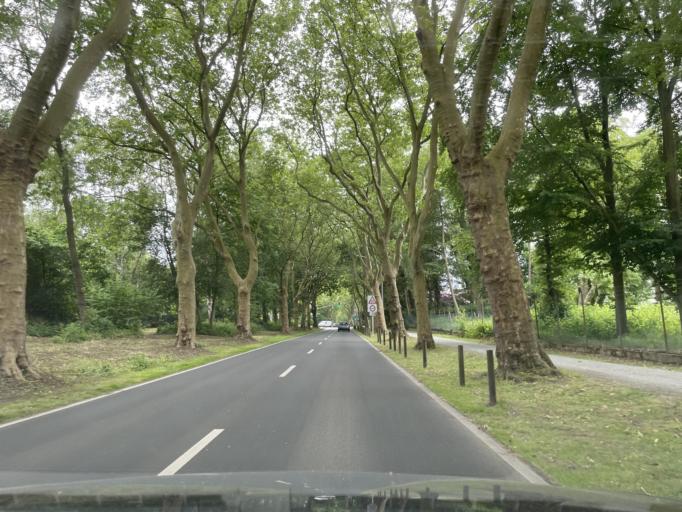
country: DE
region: North Rhine-Westphalia
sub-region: Regierungsbezirk Dusseldorf
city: Monchengladbach
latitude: 51.1558
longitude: 6.4239
